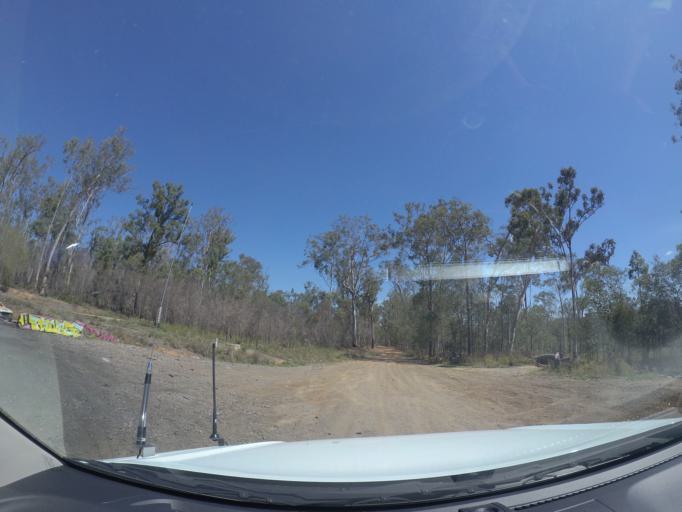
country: AU
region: Queensland
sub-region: Logan
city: North Maclean
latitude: -27.7762
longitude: 152.9370
